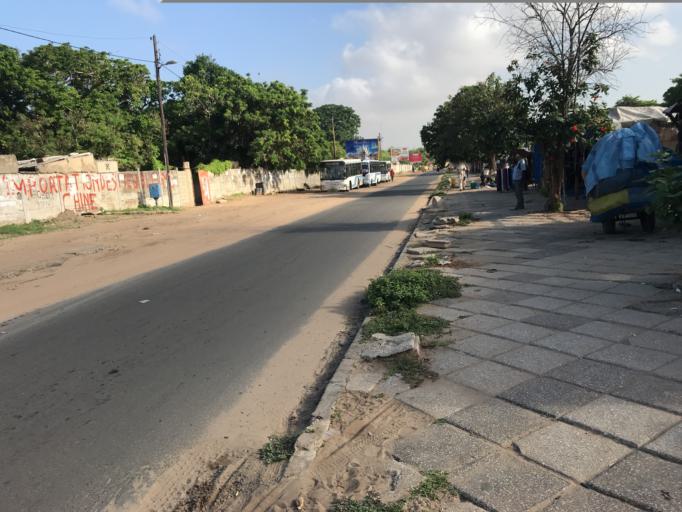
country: SN
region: Dakar
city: Dakar
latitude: 14.6833
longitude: -17.4608
